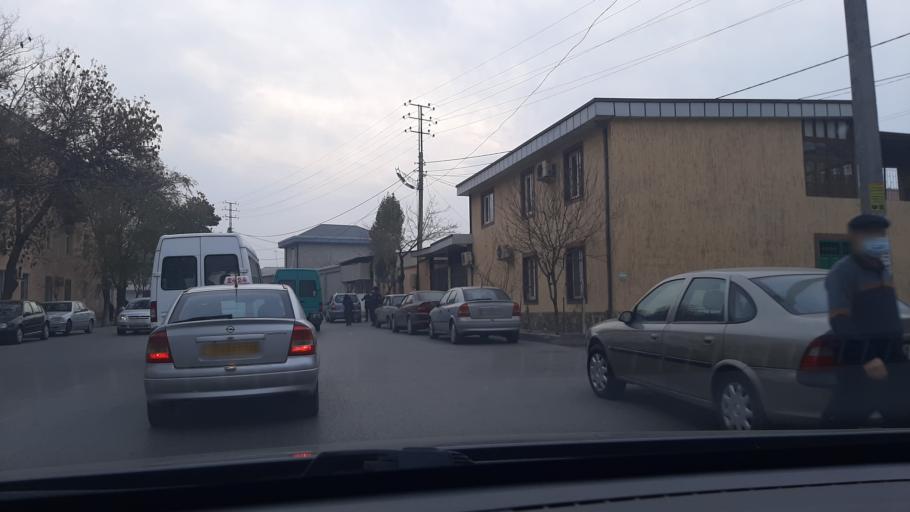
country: TJ
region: Viloyati Sughd
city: Khujand
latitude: 40.2732
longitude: 69.6389
